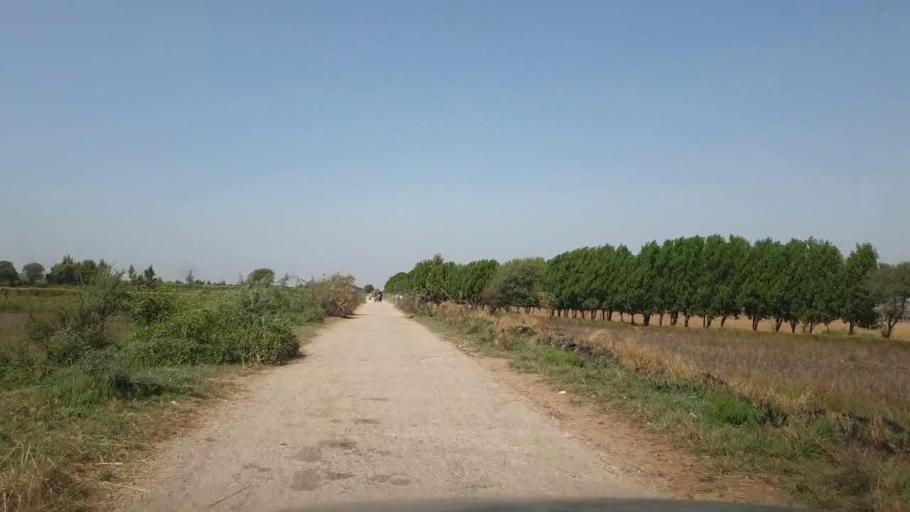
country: PK
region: Sindh
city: Tando Muhammad Khan
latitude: 25.1562
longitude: 68.3950
